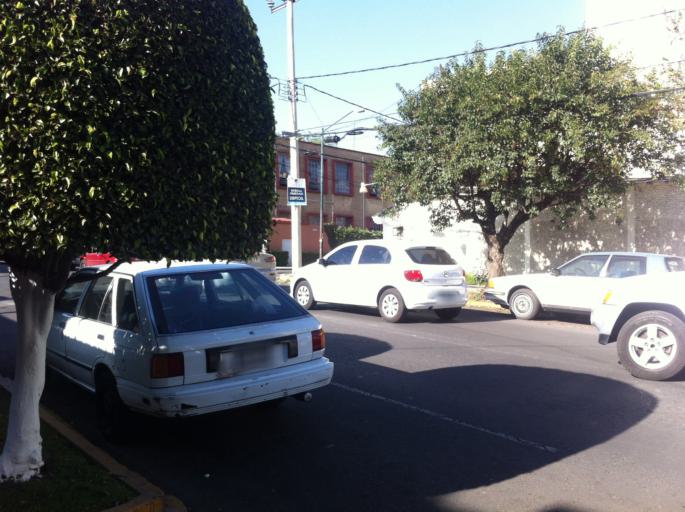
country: MX
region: Mexico
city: Colonia Lindavista
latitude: 19.4956
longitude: -99.1290
